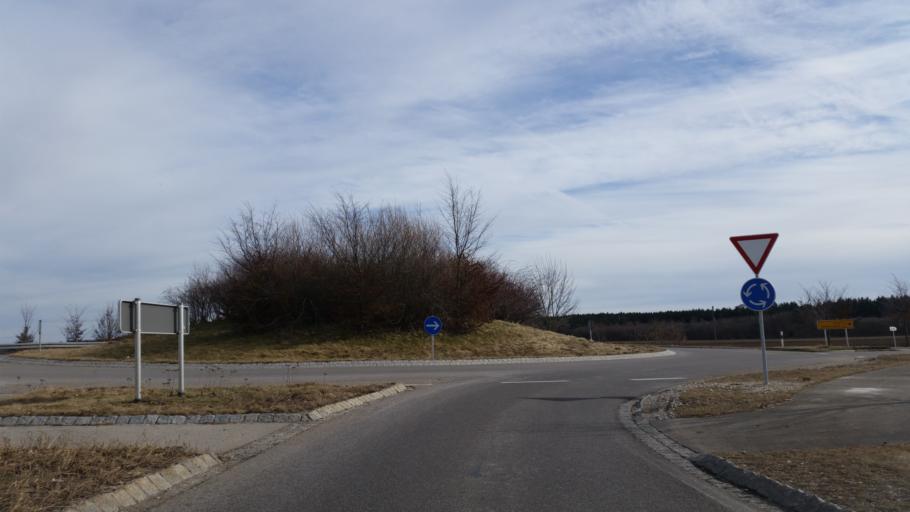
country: DE
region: Bavaria
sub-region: Upper Bavaria
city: Zorneding
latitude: 48.0741
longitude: 11.8240
